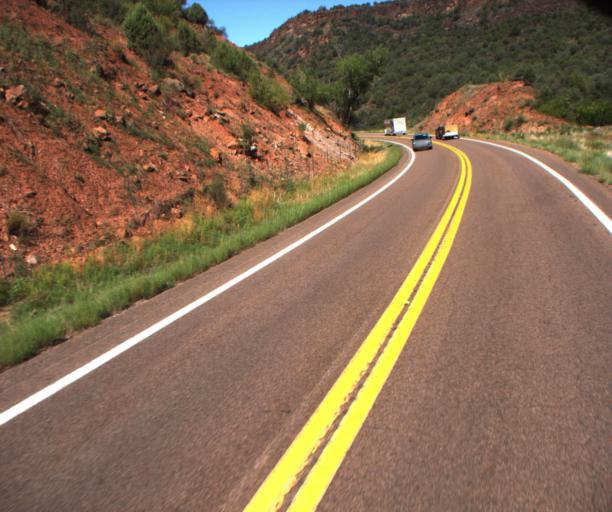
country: US
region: Arizona
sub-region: Navajo County
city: Cibecue
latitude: 34.0020
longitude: -110.2673
